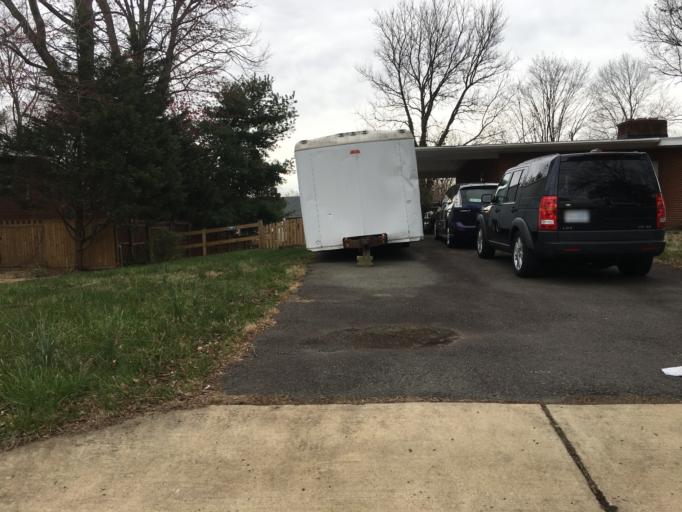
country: US
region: Virginia
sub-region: Fairfax County
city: Lake Barcroft
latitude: 38.8538
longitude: -77.1460
